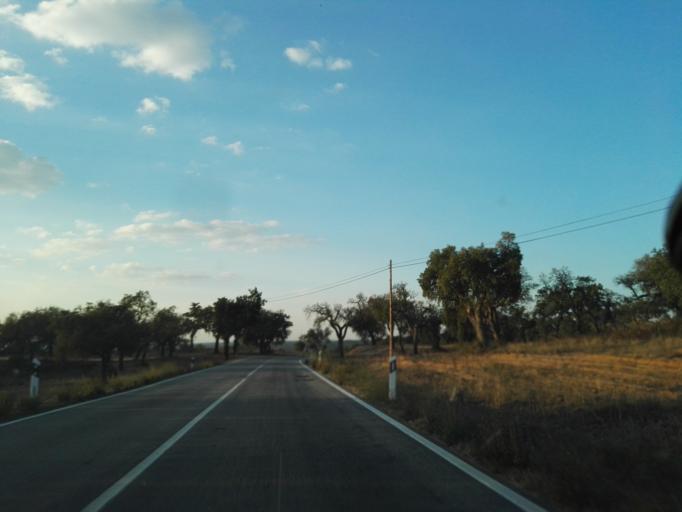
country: PT
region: Evora
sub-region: Mora
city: Mora
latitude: 38.9354
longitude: -8.1241
